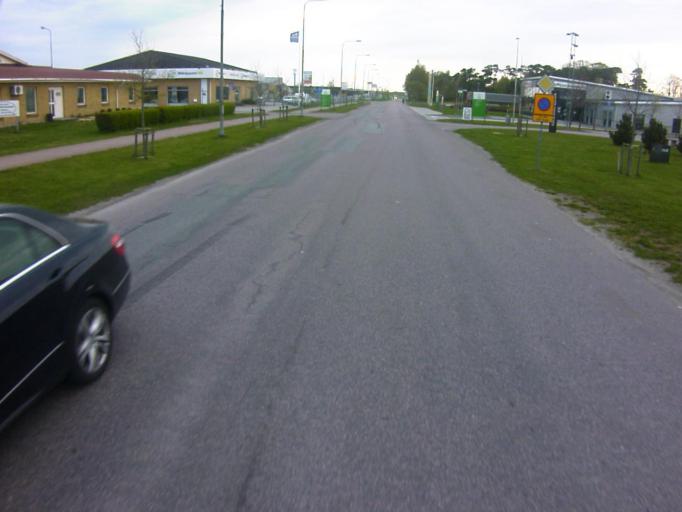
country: SE
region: Skane
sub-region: Kavlinge Kommun
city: Loddekopinge
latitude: 55.7666
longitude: 12.9981
